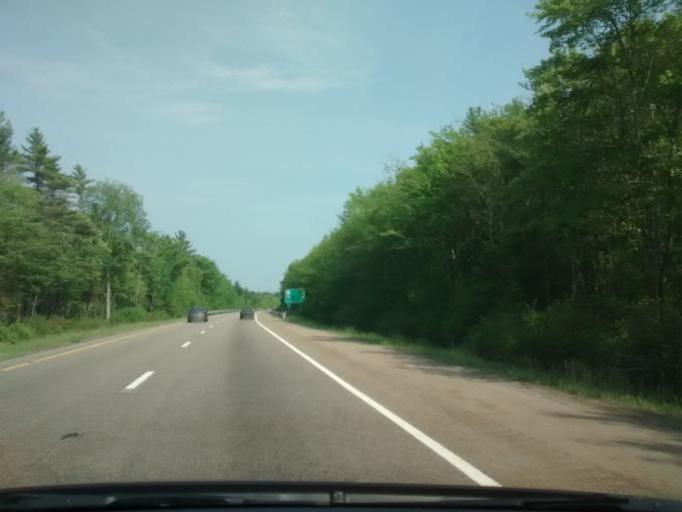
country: US
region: Massachusetts
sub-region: Plymouth County
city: Carver
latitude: 41.8431
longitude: -70.8364
